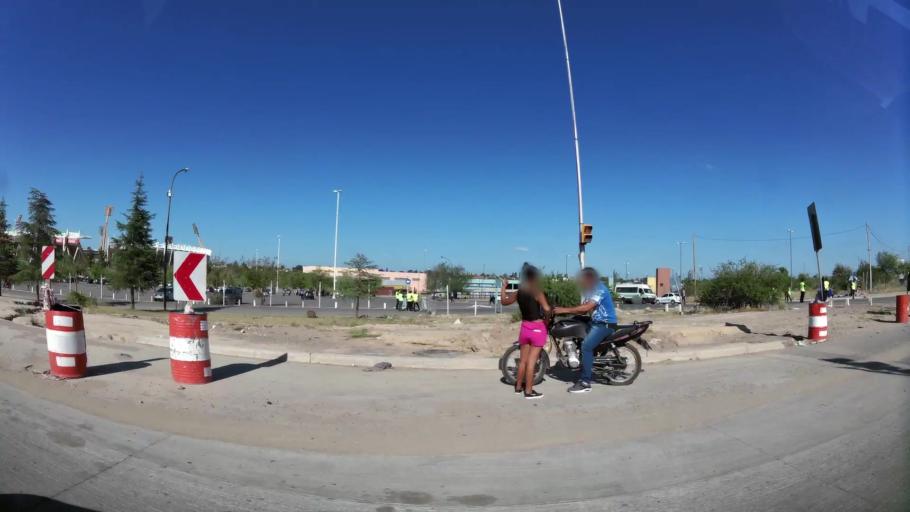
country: AR
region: Cordoba
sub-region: Departamento de Capital
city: Cordoba
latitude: -31.3711
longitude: -64.2503
